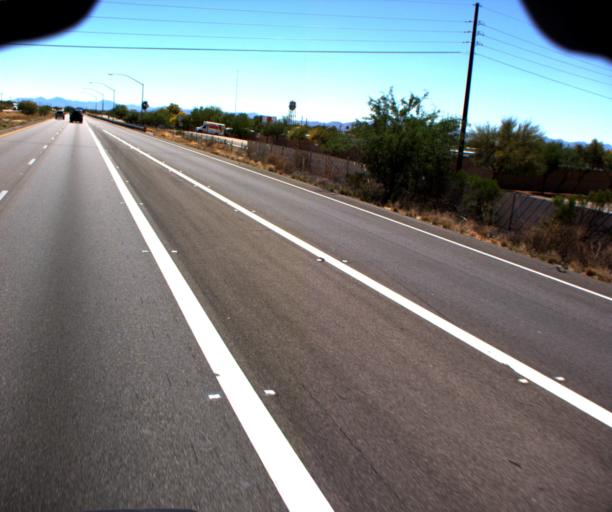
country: US
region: Arizona
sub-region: Pima County
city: Summit
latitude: 32.1012
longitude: -110.8371
